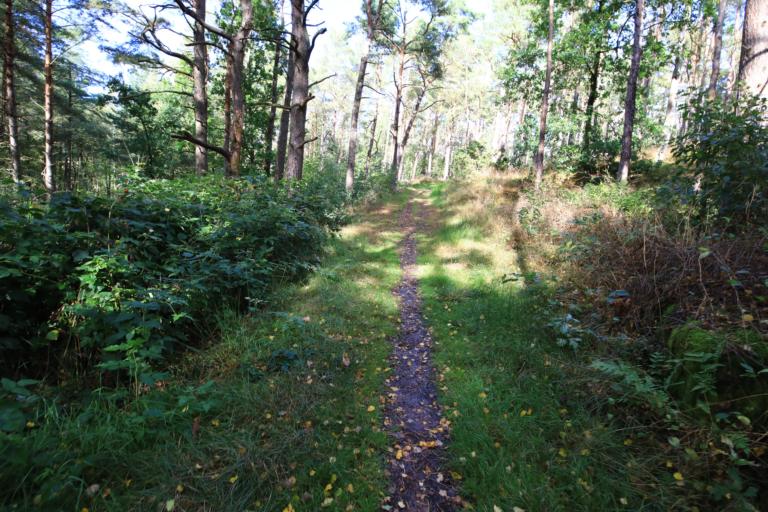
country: SE
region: Halland
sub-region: Varbergs Kommun
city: Varberg
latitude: 57.1760
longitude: 12.2166
